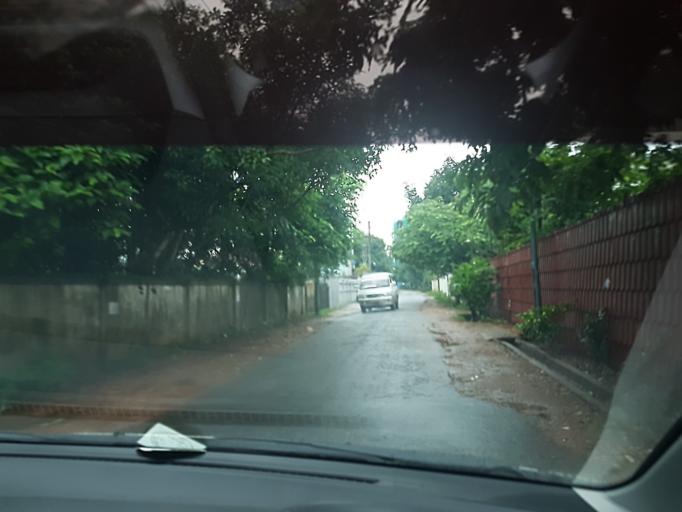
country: MM
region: Yangon
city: Yangon
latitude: 16.8053
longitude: 96.1689
